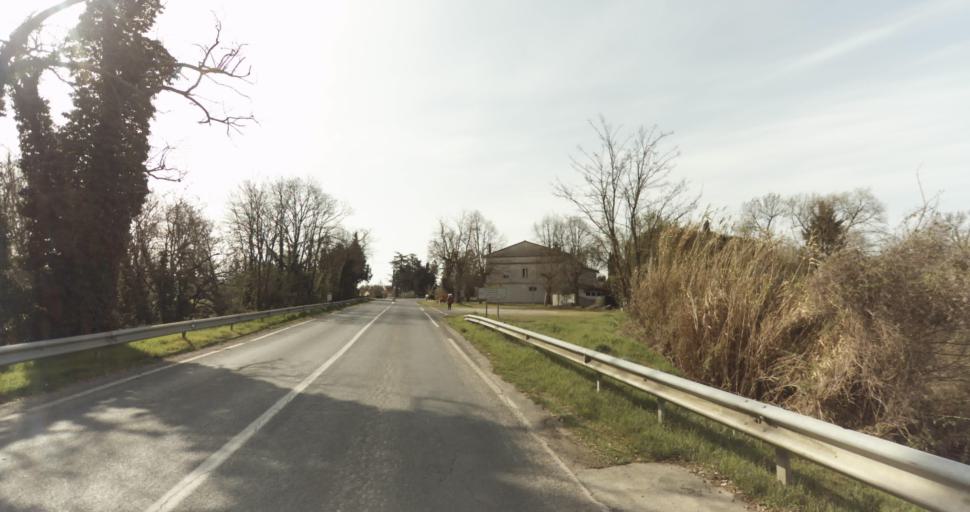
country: FR
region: Midi-Pyrenees
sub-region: Departement du Tarn
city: Saint-Sulpice-la-Pointe
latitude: 43.7843
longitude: 1.6788
